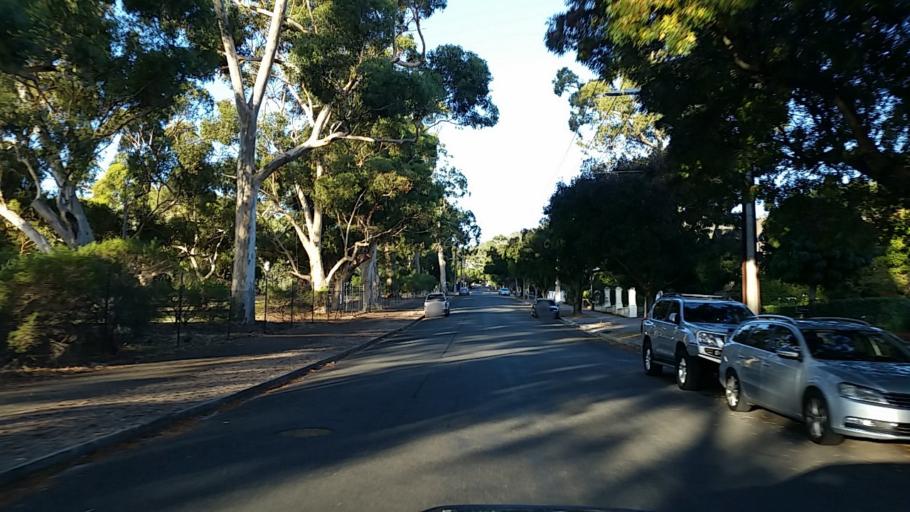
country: AU
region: South Australia
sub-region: Mitcham
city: Mitcham
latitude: -34.9706
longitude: 138.6307
